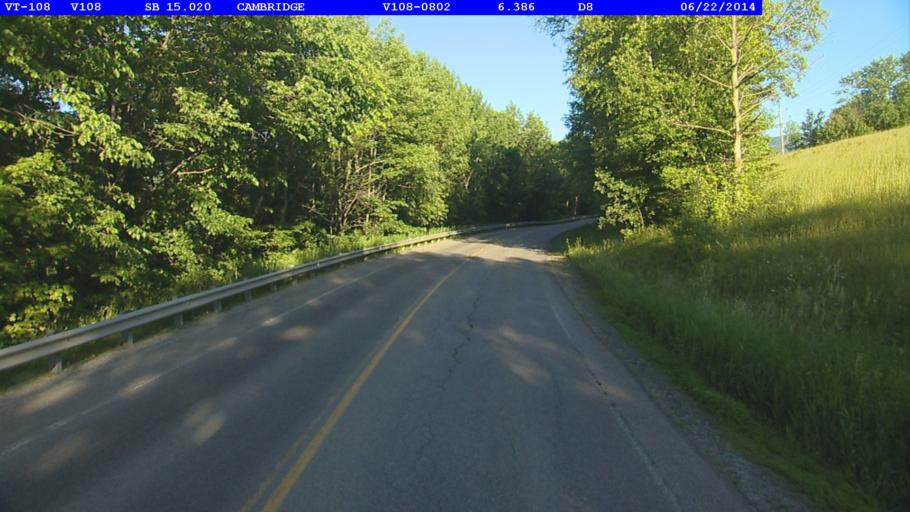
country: US
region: Vermont
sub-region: Lamoille County
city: Johnson
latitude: 44.6155
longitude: -72.8160
